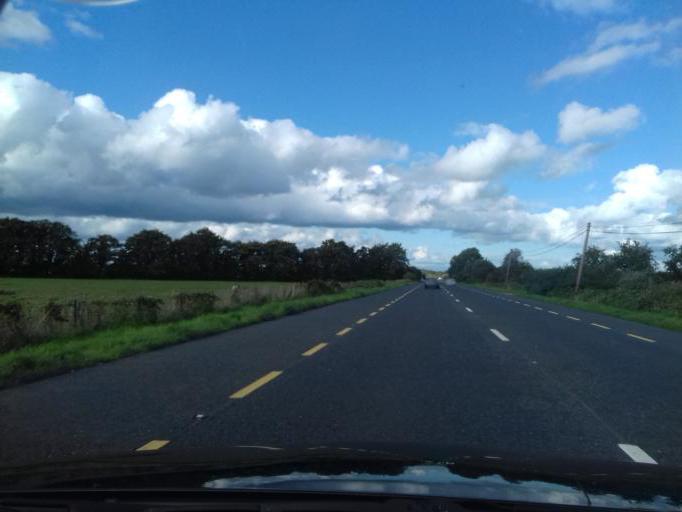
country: IE
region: Leinster
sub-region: An Iarmhi
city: Kilbeggan
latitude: 53.3446
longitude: -7.5028
